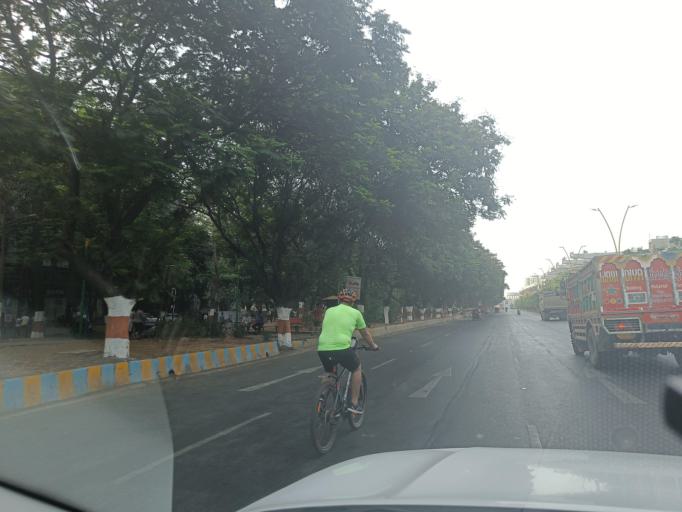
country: IN
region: Maharashtra
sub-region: Thane
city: Thane
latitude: 19.1948
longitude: 72.9627
